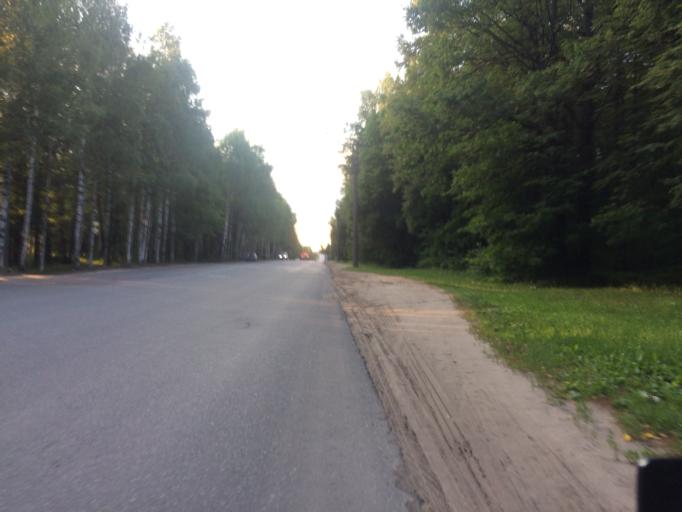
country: RU
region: Mariy-El
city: Yoshkar-Ola
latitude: 56.6233
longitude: 47.9546
